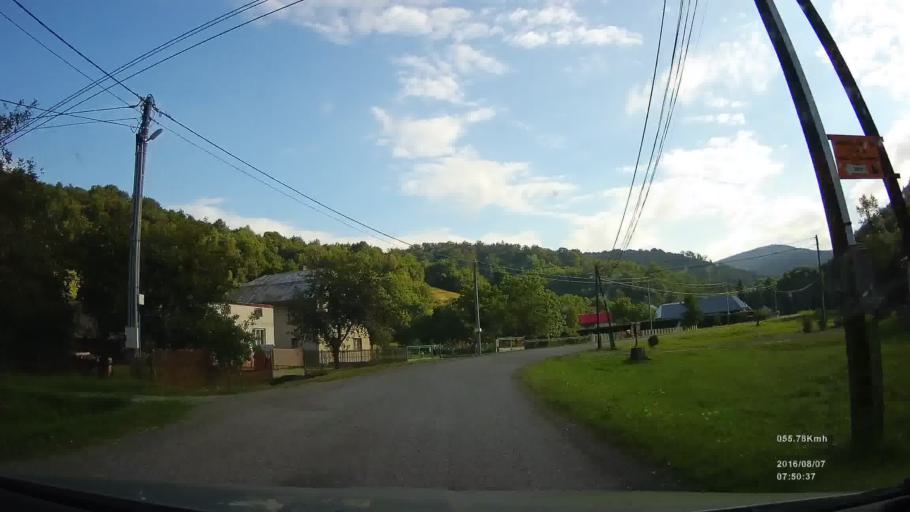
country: SK
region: Presovsky
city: Medzilaborce
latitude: 49.3008
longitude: 21.7781
